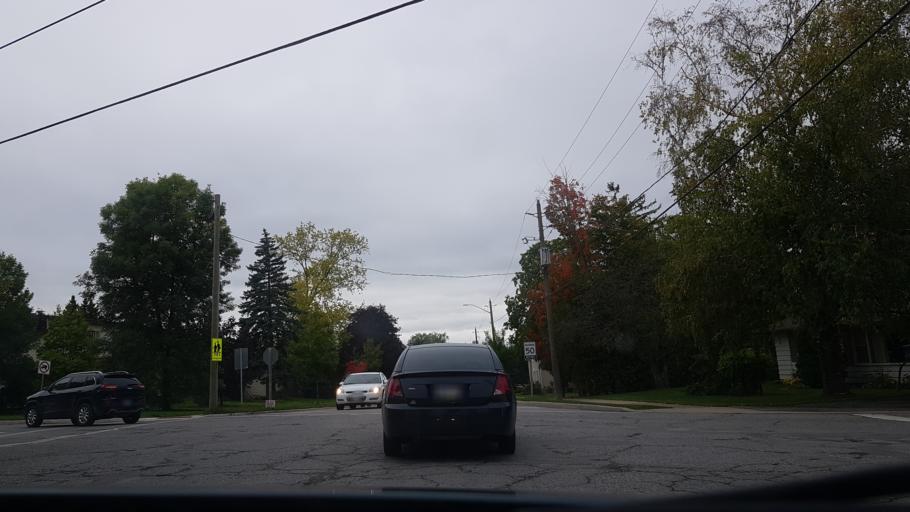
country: CA
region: Ontario
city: Uxbridge
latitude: 44.0995
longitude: -78.9558
